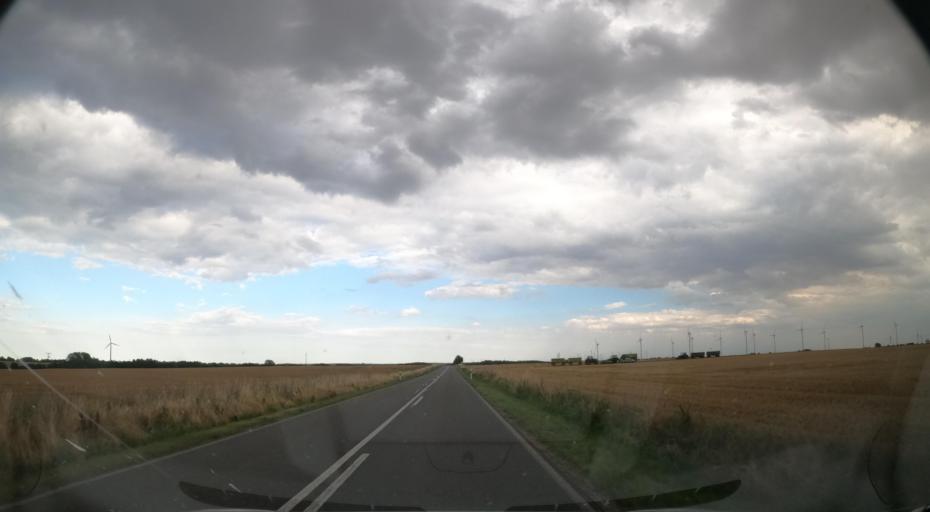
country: DE
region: Mecklenburg-Vorpommern
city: Strasburg
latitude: 53.4897
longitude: 13.8365
